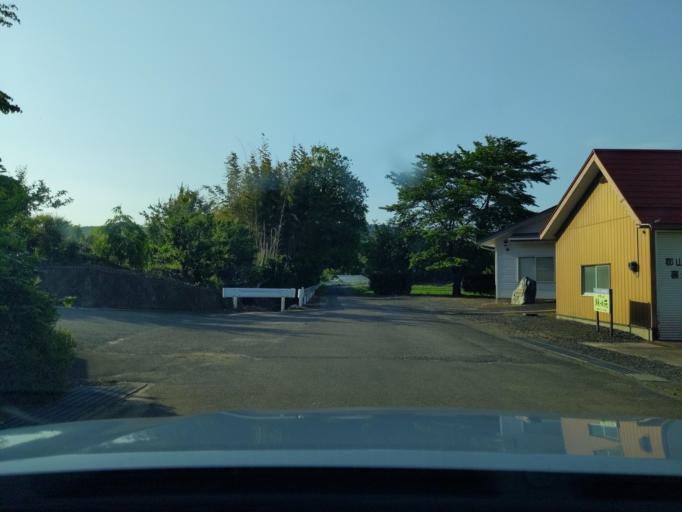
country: JP
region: Fukushima
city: Motomiya
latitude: 37.4711
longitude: 140.3301
